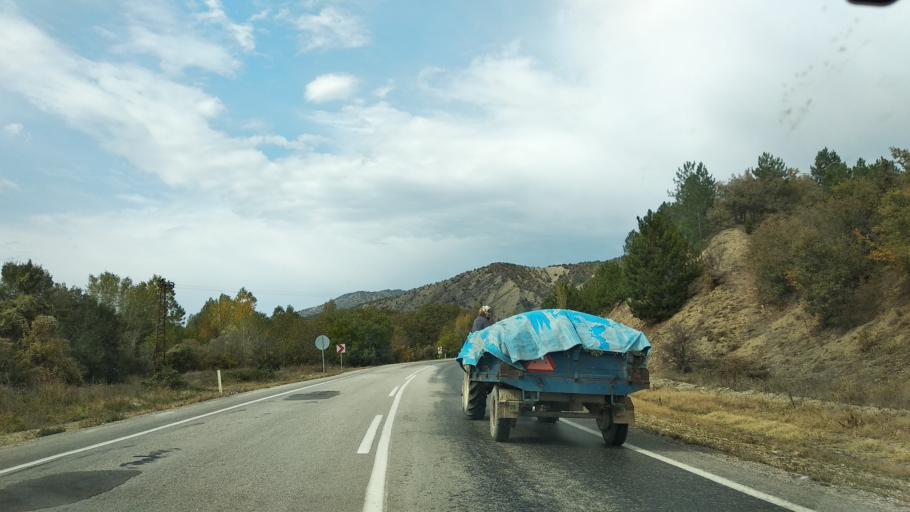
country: TR
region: Ankara
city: Nallihan
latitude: 40.3087
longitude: 31.2715
